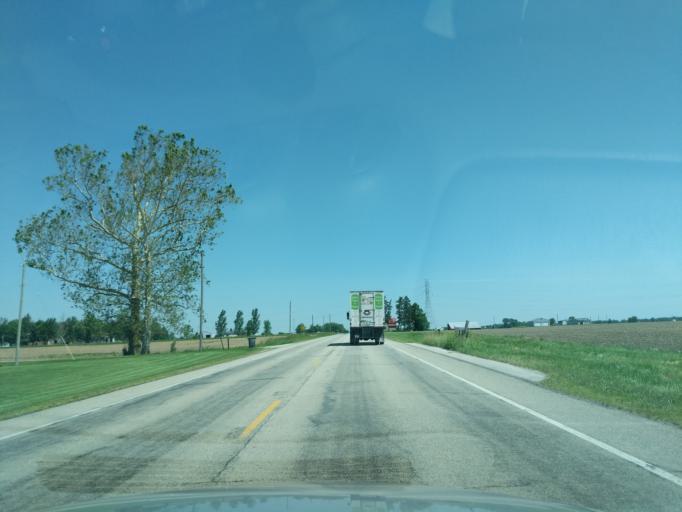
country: US
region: Indiana
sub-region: Whitley County
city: Columbia City
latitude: 41.0602
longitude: -85.4705
